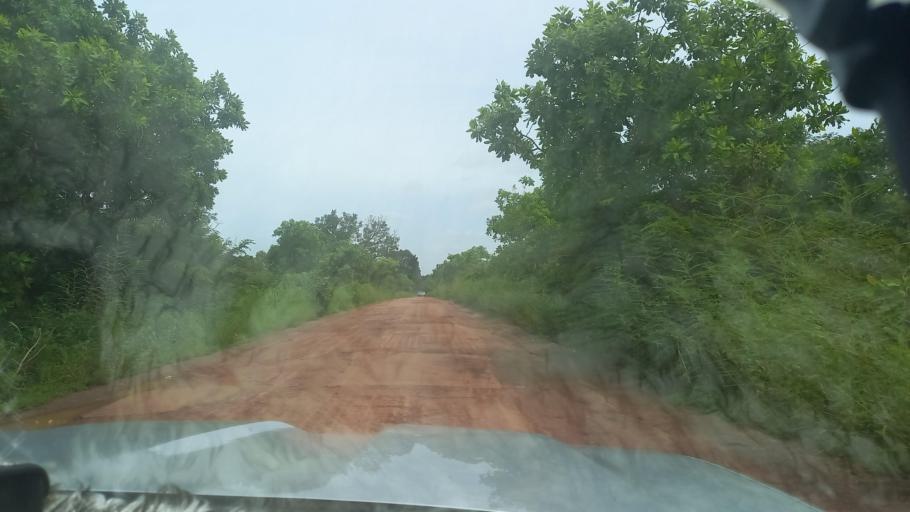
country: SN
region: Kolda
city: Marsassoum
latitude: 12.9033
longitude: -16.0219
